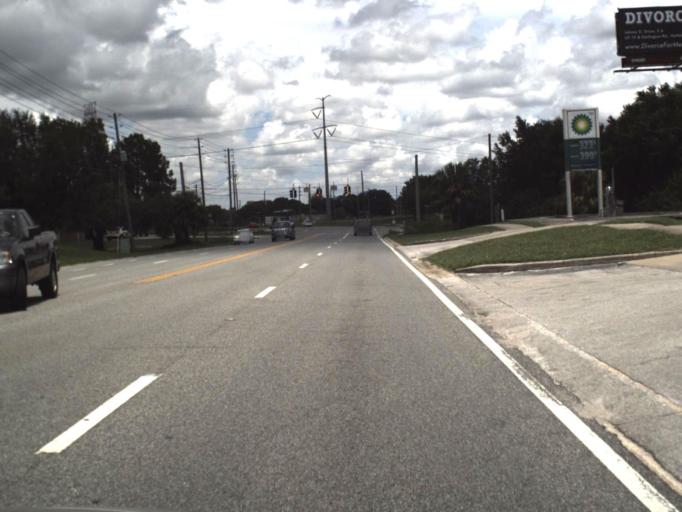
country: US
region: Florida
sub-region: Pasco County
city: Trinity
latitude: 28.2012
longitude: -82.6956
